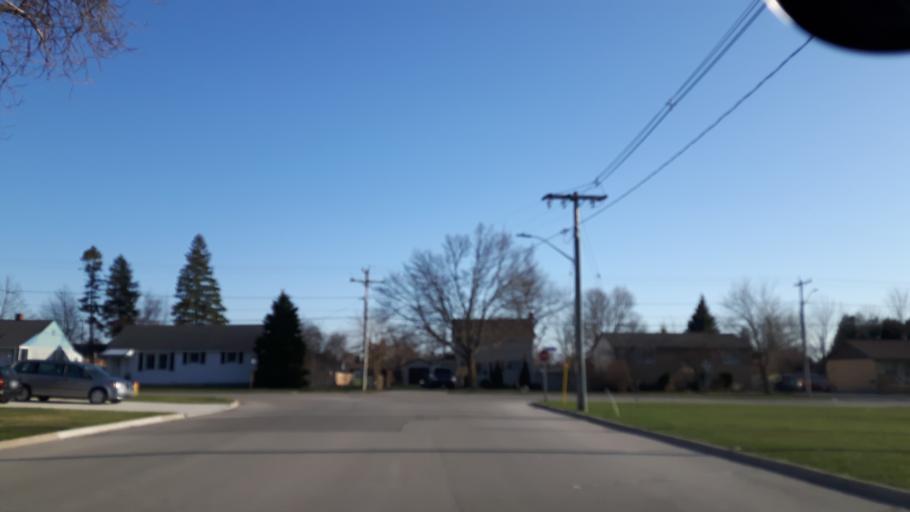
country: CA
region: Ontario
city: Goderich
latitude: 43.7359
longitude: -81.7138
